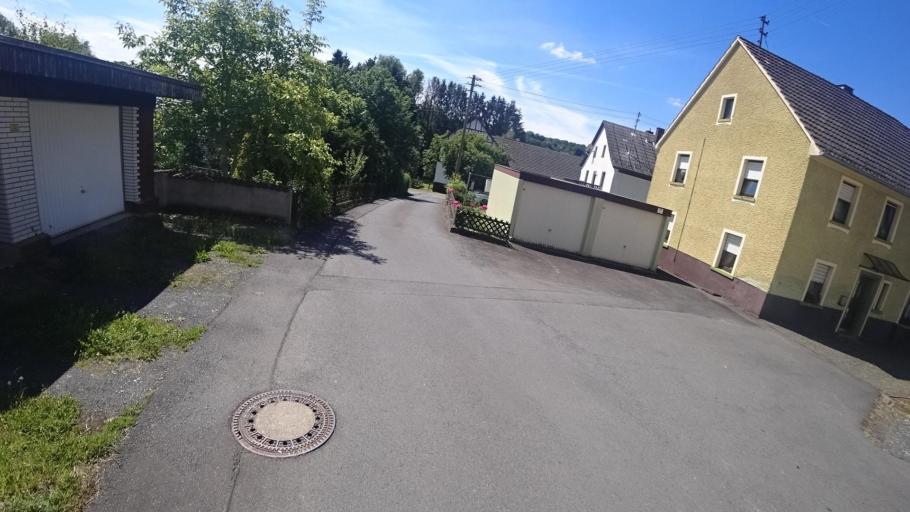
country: DE
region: Rheinland-Pfalz
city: Sorth
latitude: 50.6989
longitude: 7.6844
